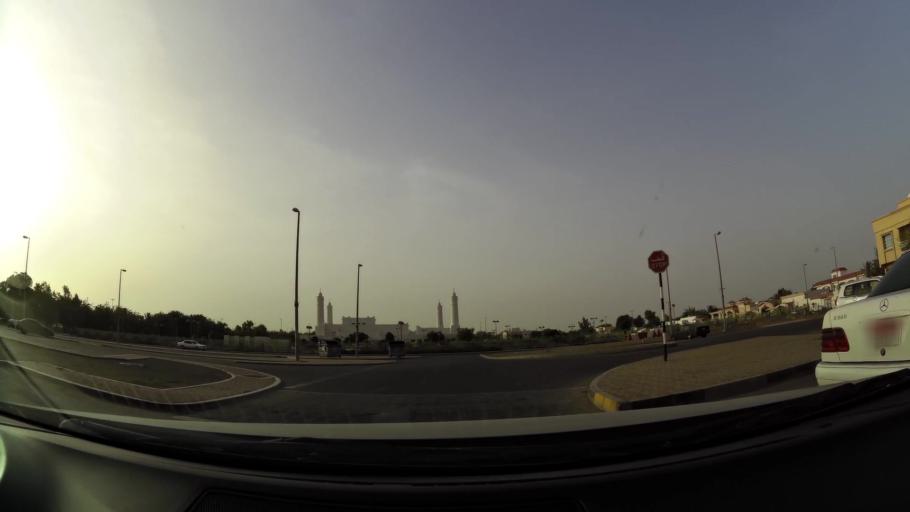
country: OM
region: Al Buraimi
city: Al Buraymi
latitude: 24.2424
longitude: 55.7406
